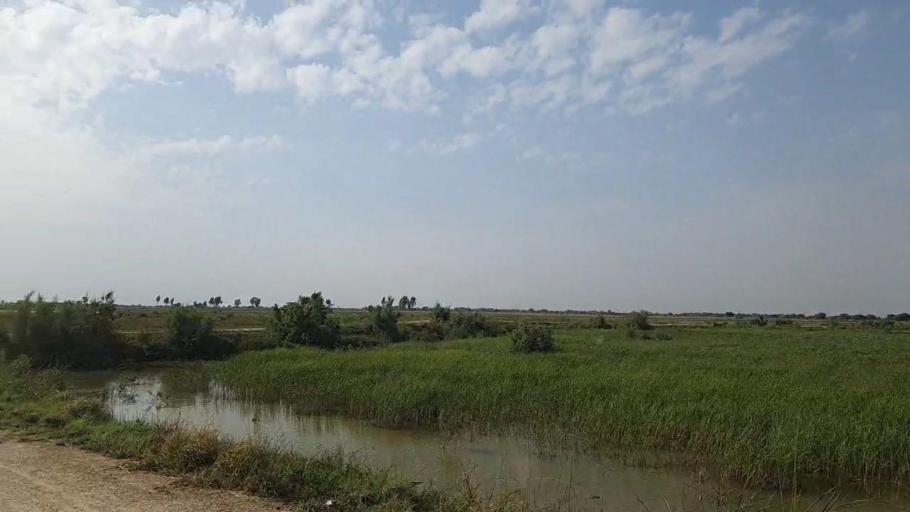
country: PK
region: Sindh
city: Daro Mehar
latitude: 24.7622
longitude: 68.1667
